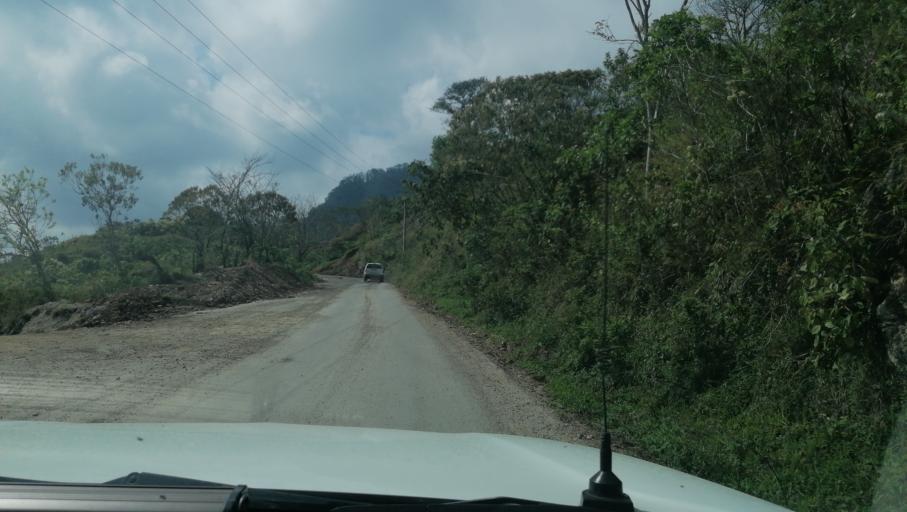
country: MX
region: Chiapas
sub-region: Ocotepec
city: San Pablo Huacano
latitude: 17.2517
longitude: -93.2693
